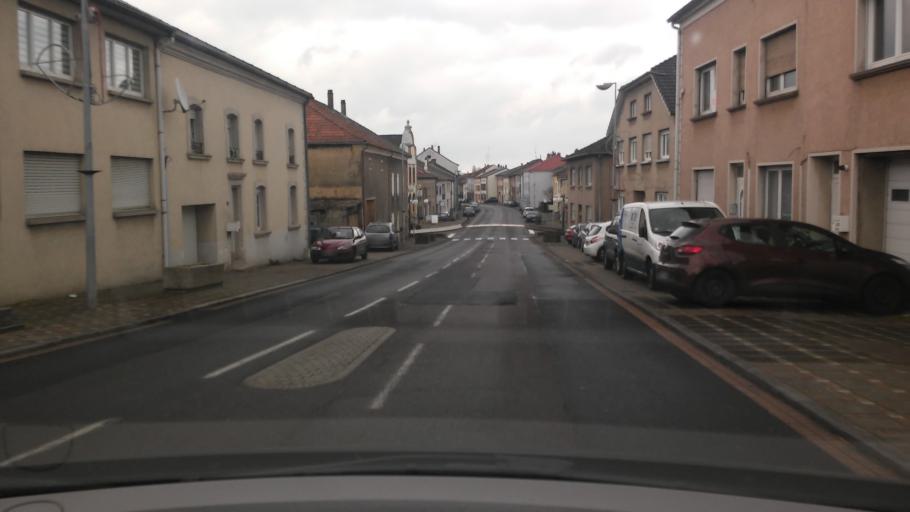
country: FR
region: Lorraine
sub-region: Departement de la Moselle
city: Longeville-les-Saint-Avold
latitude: 49.1147
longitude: 6.6358
